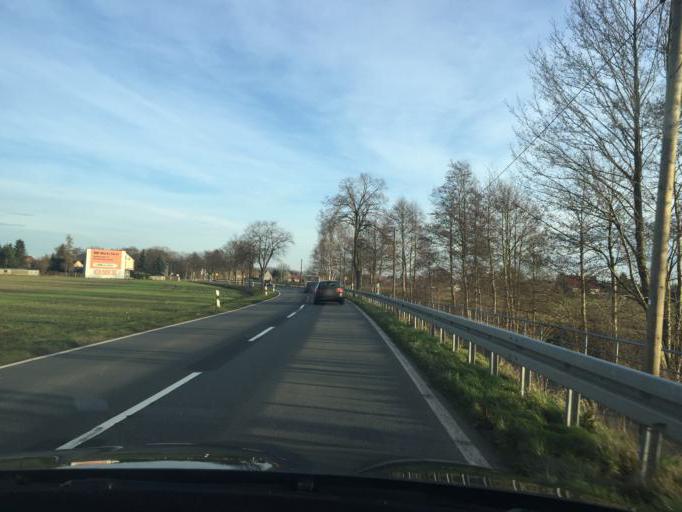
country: DE
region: Brandenburg
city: Forst
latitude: 51.7220
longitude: 14.6034
